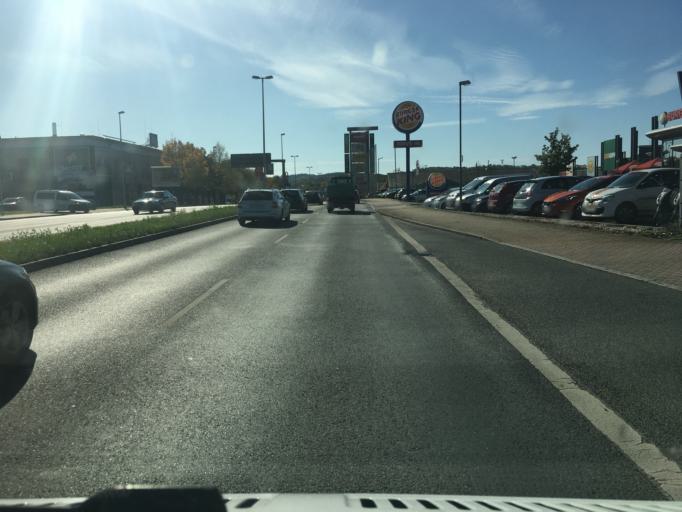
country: DE
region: Saxony
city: Zwickau
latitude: 50.7086
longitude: 12.5021
